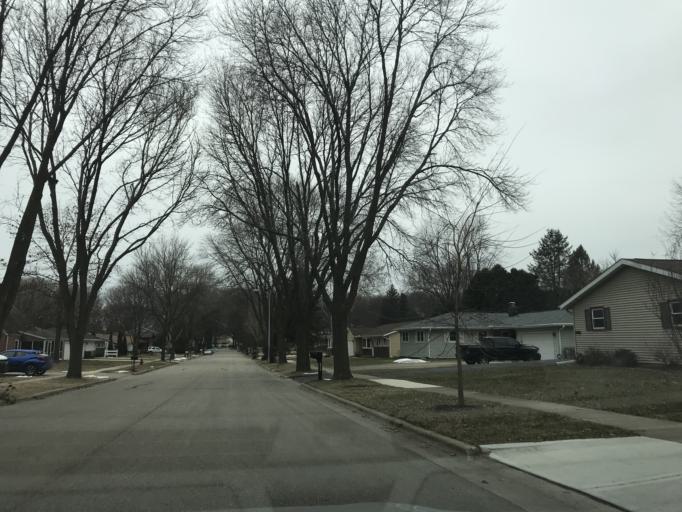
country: US
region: Wisconsin
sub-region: Dane County
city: Monona
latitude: 43.1007
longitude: -89.3022
